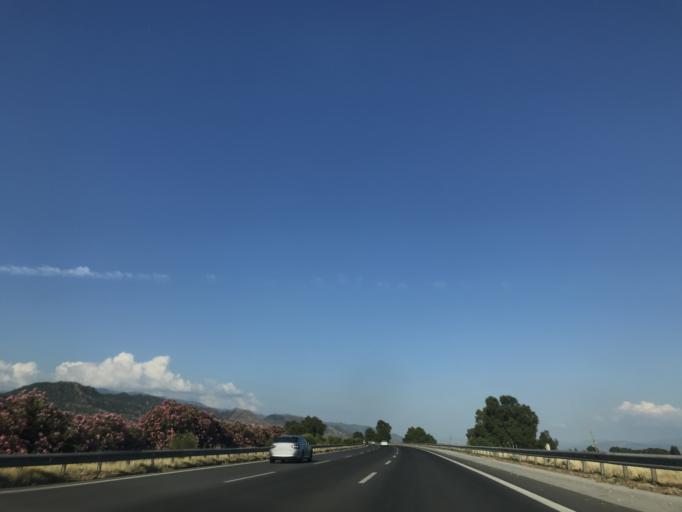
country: TR
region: Aydin
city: Germencik
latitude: 37.8692
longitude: 27.6534
